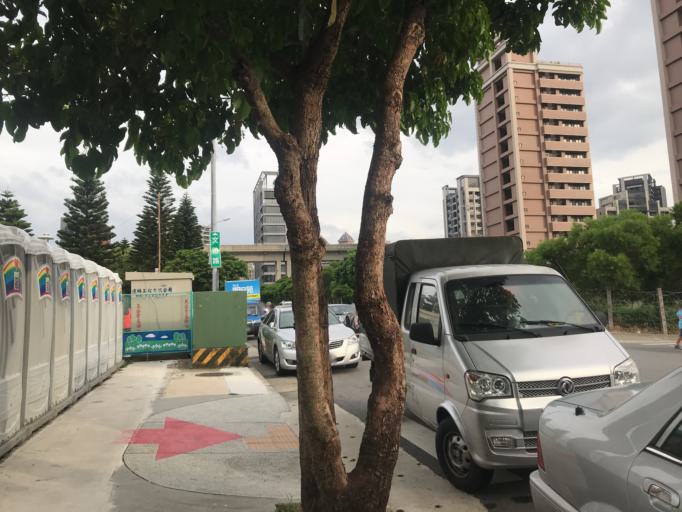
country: TW
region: Taiwan
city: Taoyuan City
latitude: 25.0050
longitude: 121.2045
